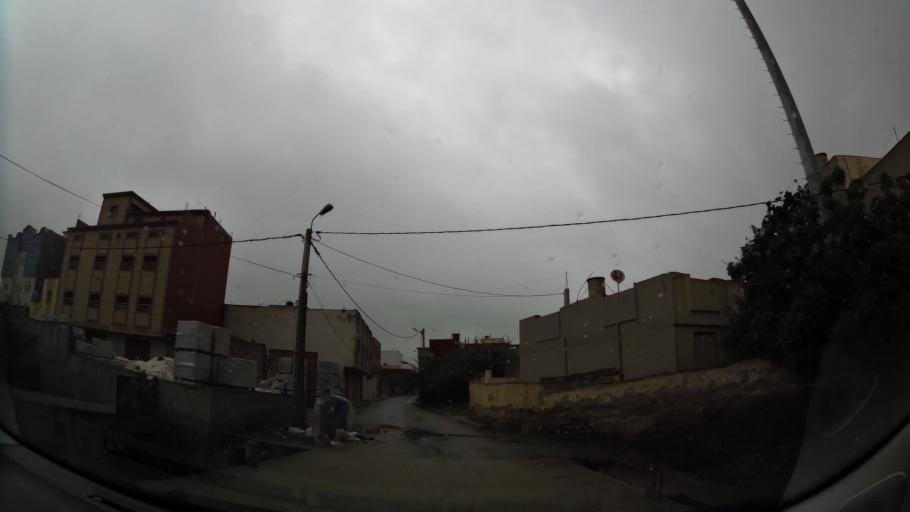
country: MA
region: Oriental
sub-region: Nador
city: Nador
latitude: 35.1591
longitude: -2.9526
